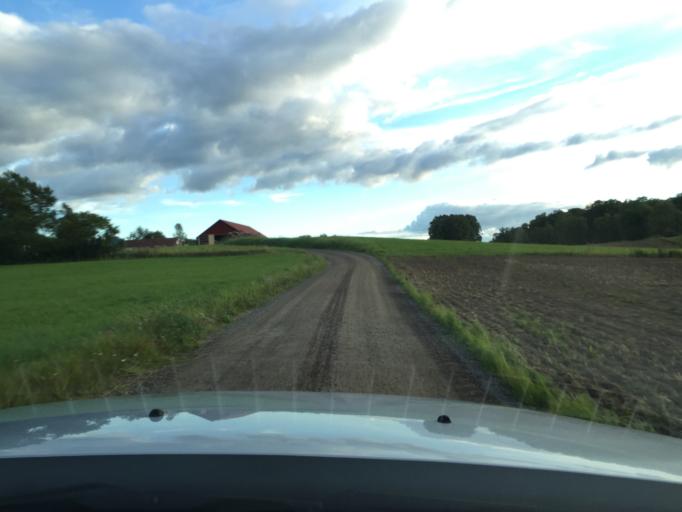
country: SE
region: Skane
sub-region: Hassleholms Kommun
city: Sosdala
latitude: 56.0393
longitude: 13.7098
